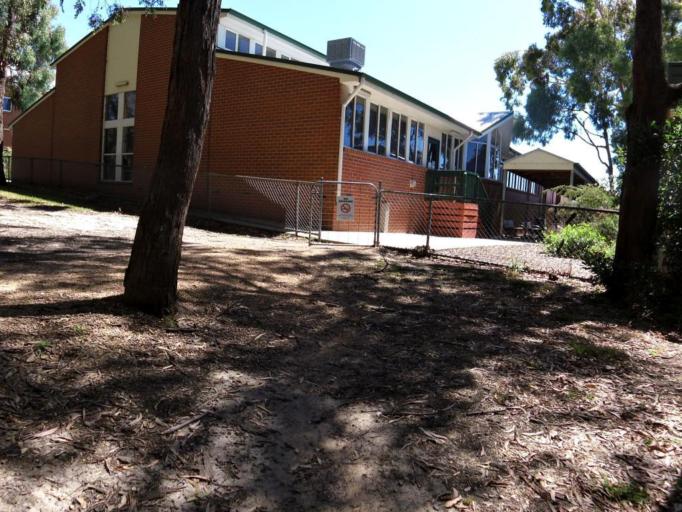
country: AU
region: Victoria
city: Mitcham
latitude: -37.8159
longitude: 145.2068
